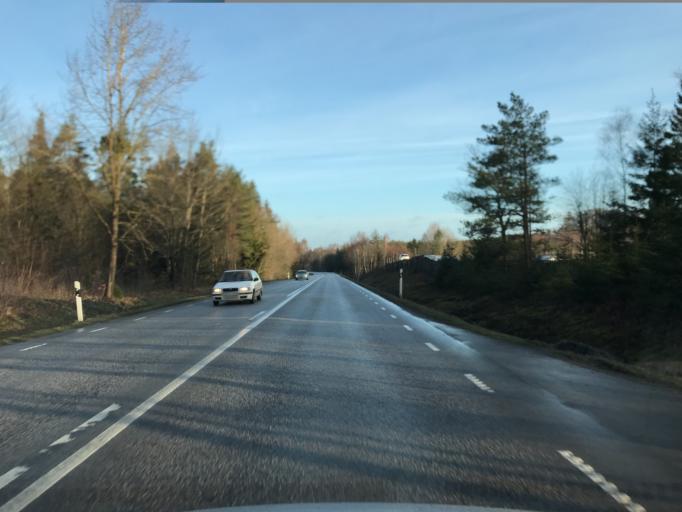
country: SE
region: Skane
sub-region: Hassleholms Kommun
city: Bjarnum
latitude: 56.2510
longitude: 13.7168
